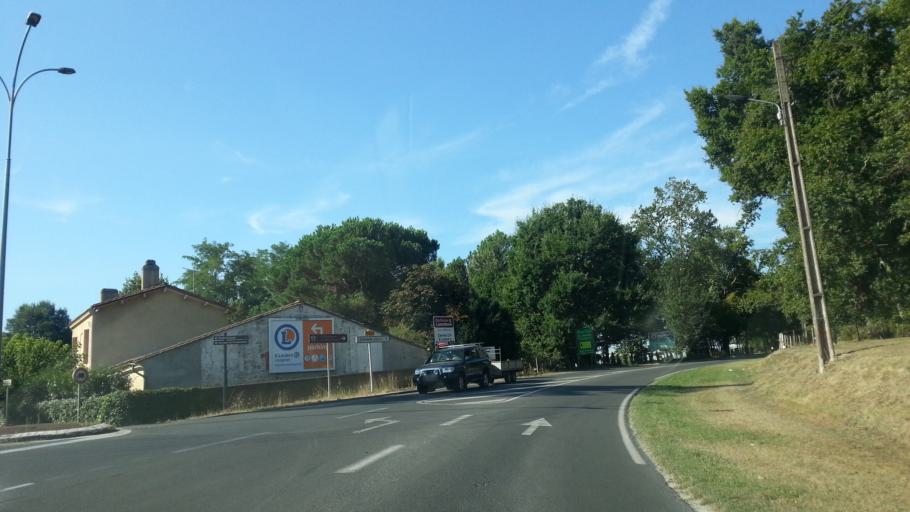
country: FR
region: Aquitaine
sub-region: Departement de la Gironde
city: Leognan
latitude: 44.7496
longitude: -0.5886
